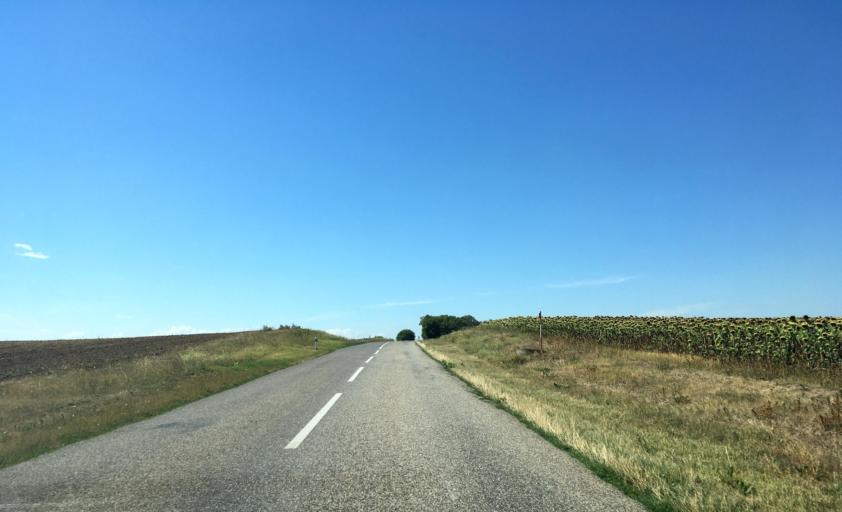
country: SK
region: Nitriansky
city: Svodin
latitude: 47.8507
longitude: 18.4421
